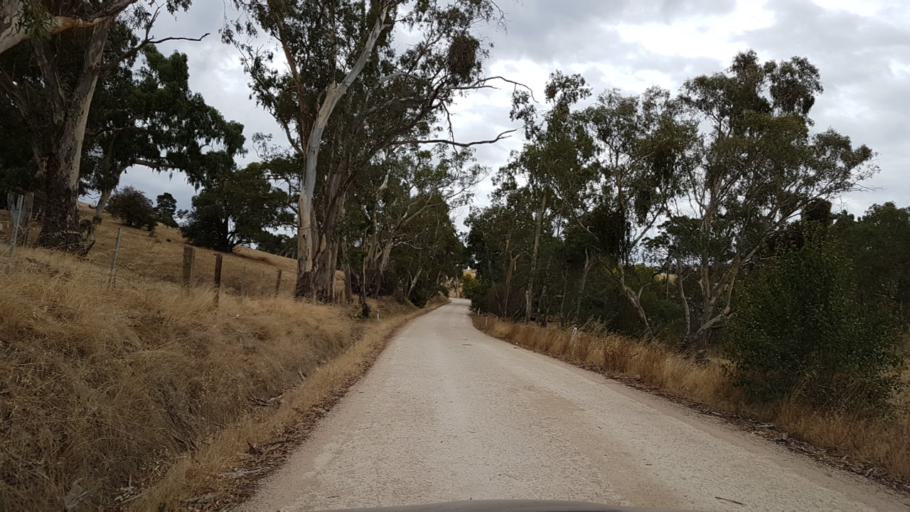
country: AU
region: South Australia
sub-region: Adelaide Hills
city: Gumeracha
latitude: -34.8067
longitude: 138.8100
